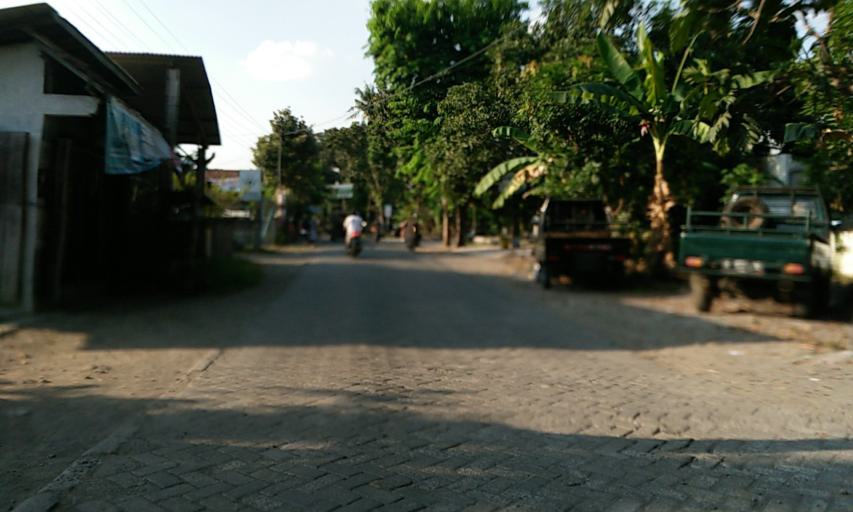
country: ID
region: Central Java
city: Mranggen
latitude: -7.0101
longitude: 110.4878
